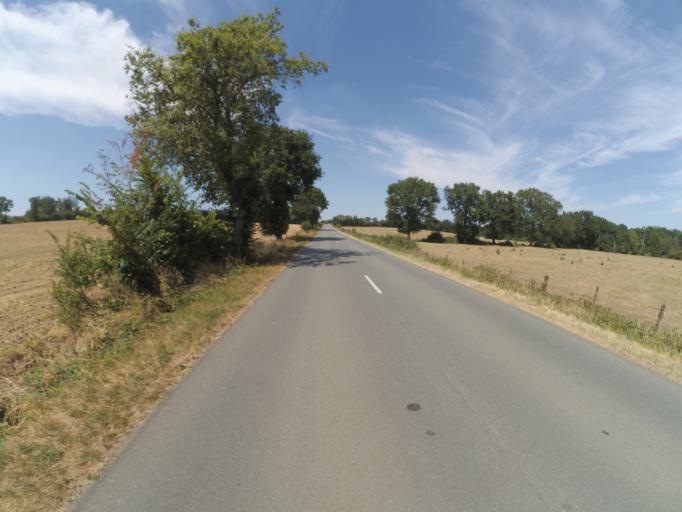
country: FR
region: Poitou-Charentes
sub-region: Departement de la Vienne
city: Usson-du-Poitou
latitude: 46.3128
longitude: 0.4937
